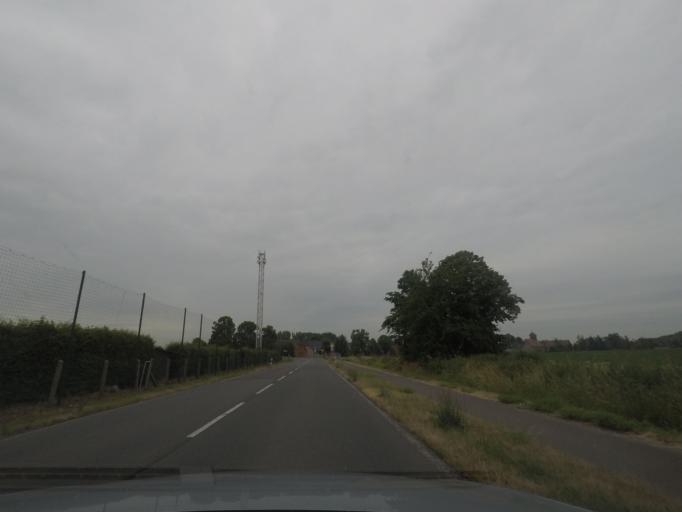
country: DE
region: Saxony-Anhalt
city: Seehausen
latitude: 52.1349
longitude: 11.2626
